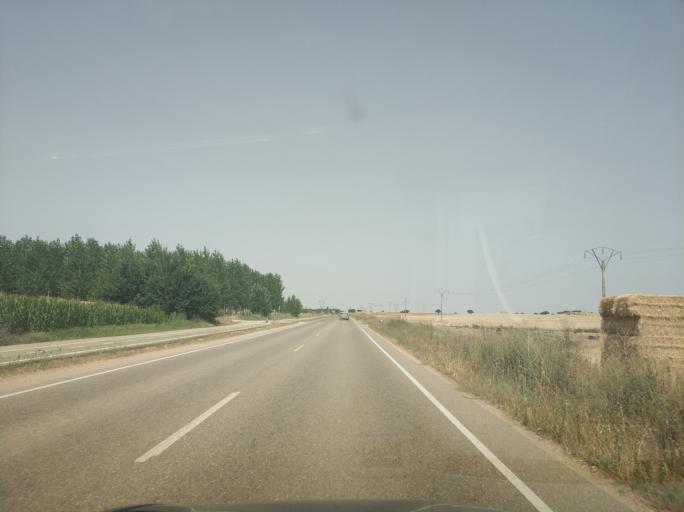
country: ES
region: Castille and Leon
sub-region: Provincia de Salamanca
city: Villamayor
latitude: 41.0237
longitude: -5.7225
